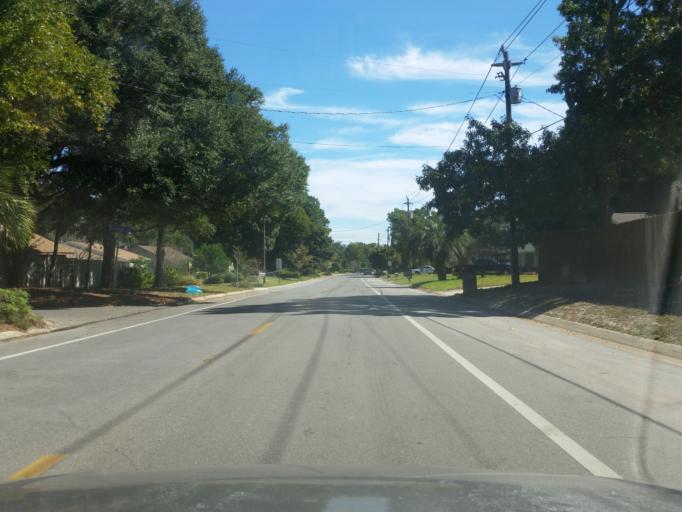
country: US
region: Florida
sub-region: Escambia County
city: East Pensacola Heights
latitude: 30.4624
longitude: -87.1744
